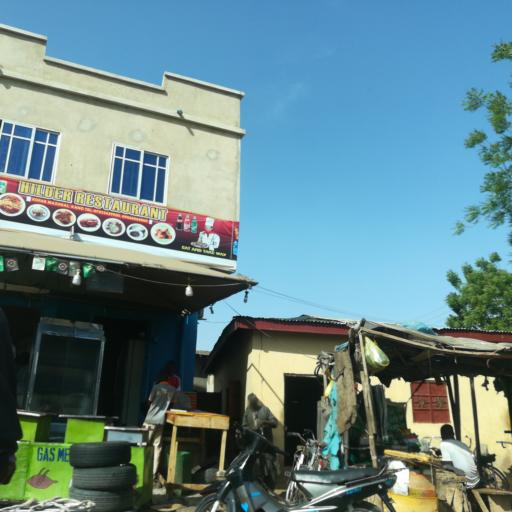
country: NG
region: Kano
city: Kano
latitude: 12.0150
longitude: 8.5184
